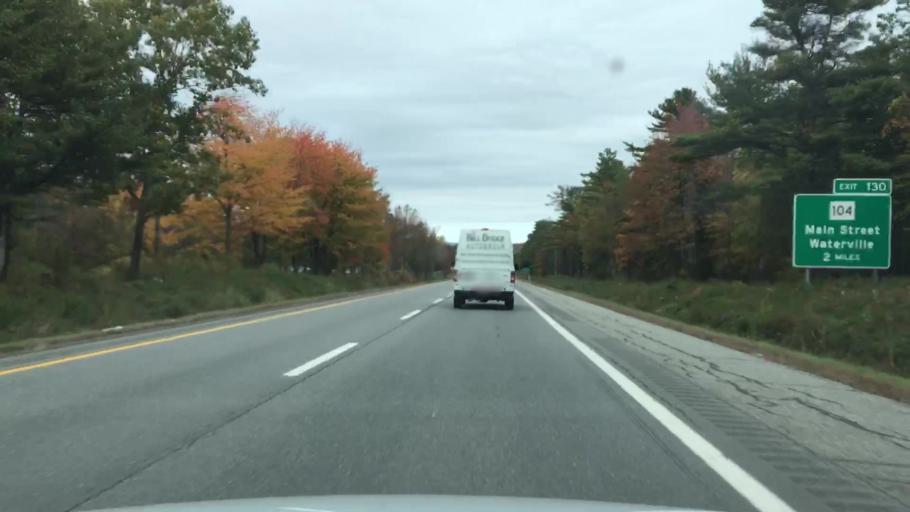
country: US
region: Maine
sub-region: Kennebec County
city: Waterville
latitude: 44.5601
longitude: -69.6725
